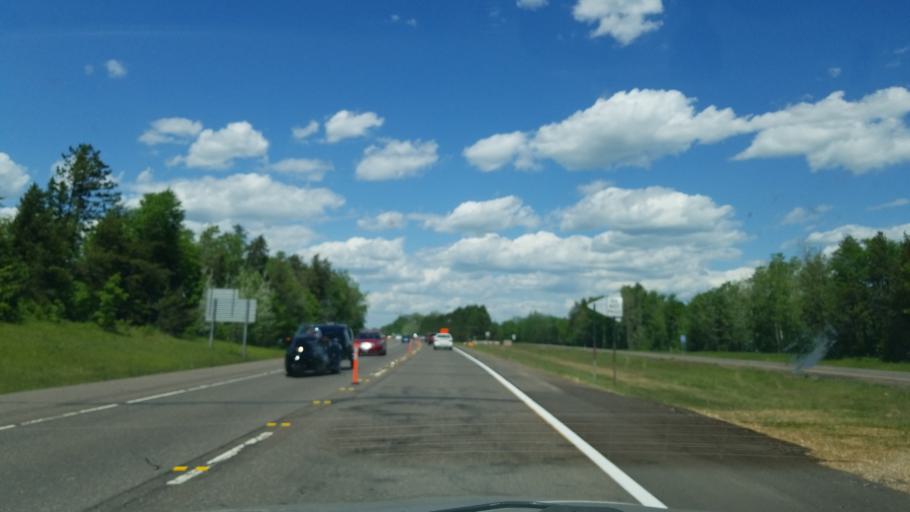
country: US
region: Minnesota
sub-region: Carlton County
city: Moose Lake
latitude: 46.3801
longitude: -92.7857
